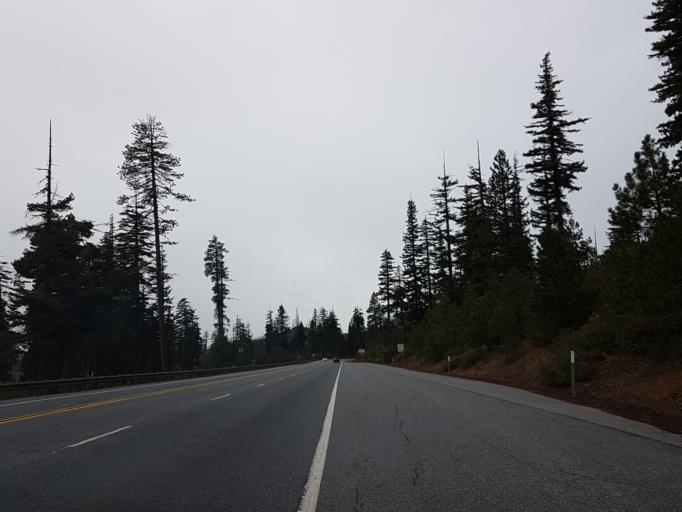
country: US
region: Oregon
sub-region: Deschutes County
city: Sisters
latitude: 44.4196
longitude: -121.7853
